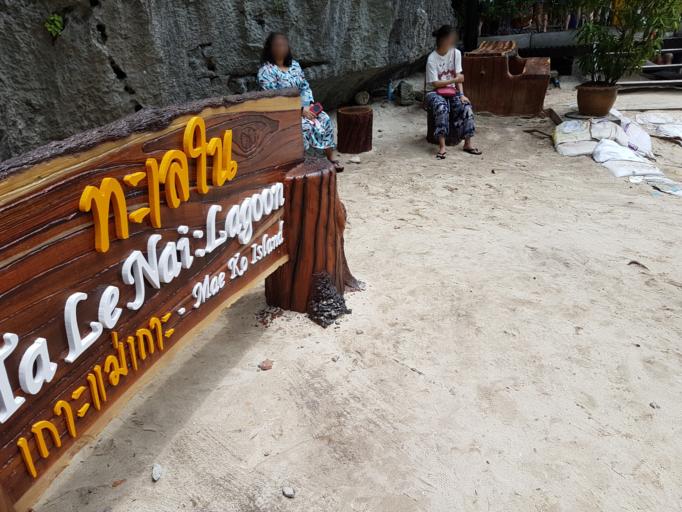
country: TH
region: Surat Thani
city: Ko Samui
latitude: 9.6581
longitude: 99.6663
